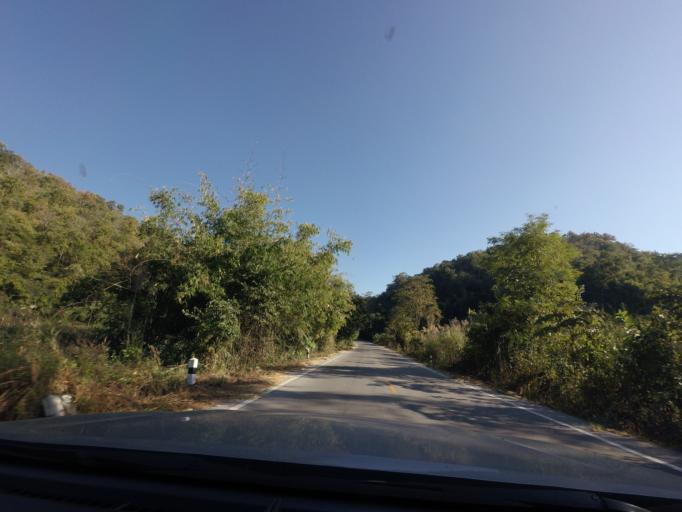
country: TH
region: Lampang
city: Chae Hom
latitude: 18.5608
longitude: 99.6256
